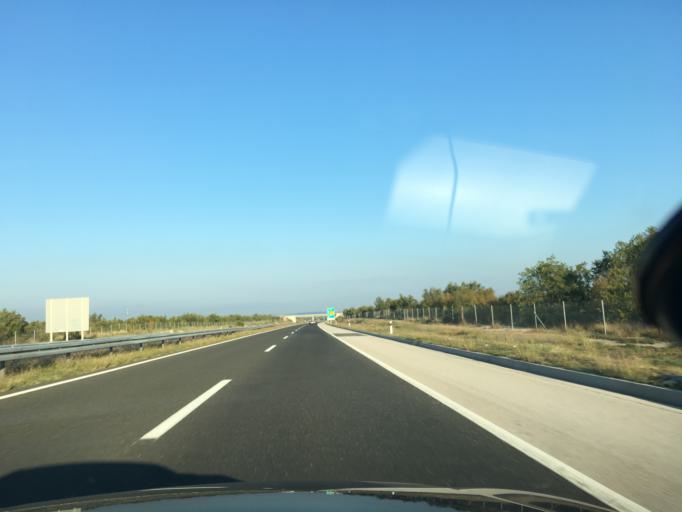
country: HR
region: Zadarska
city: Benkovac
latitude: 44.0046
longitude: 15.5963
